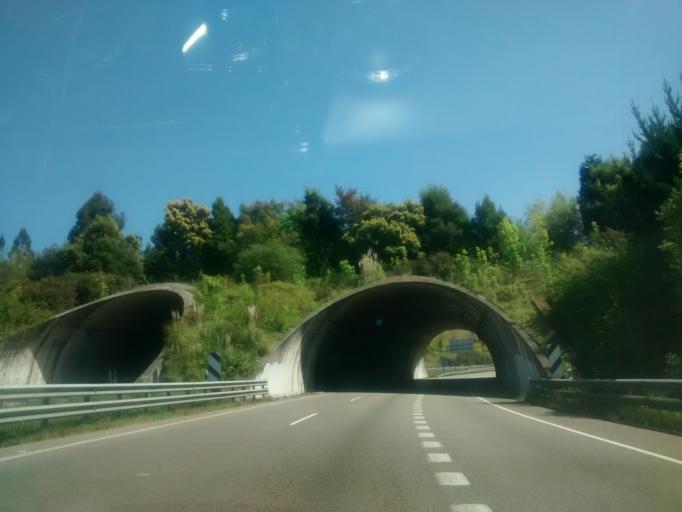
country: ES
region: Asturias
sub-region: Province of Asturias
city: Arriba
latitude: 43.5105
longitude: -5.5984
